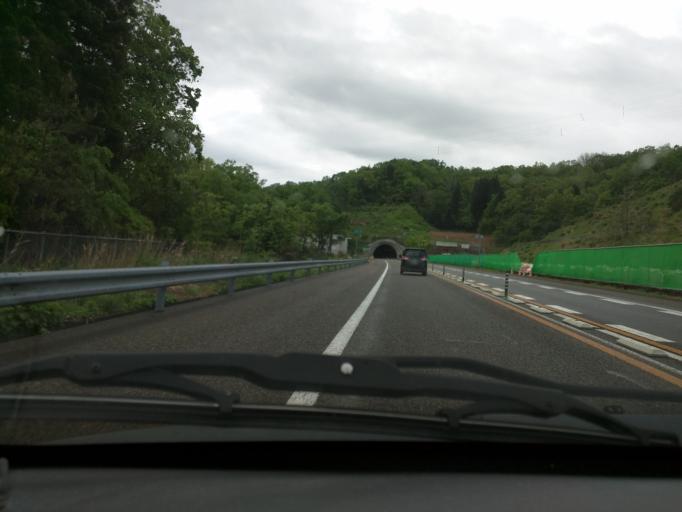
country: JP
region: Niigata
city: Joetsu
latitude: 37.1083
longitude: 138.2194
